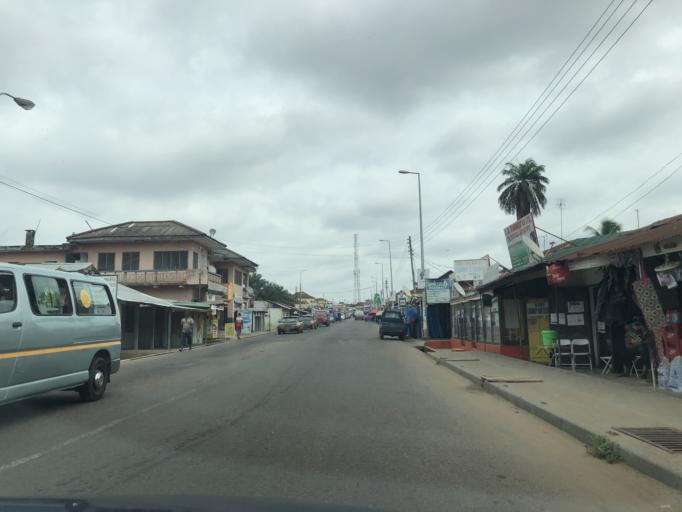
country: GH
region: Eastern
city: Koforidua
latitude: 6.0982
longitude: -0.2627
